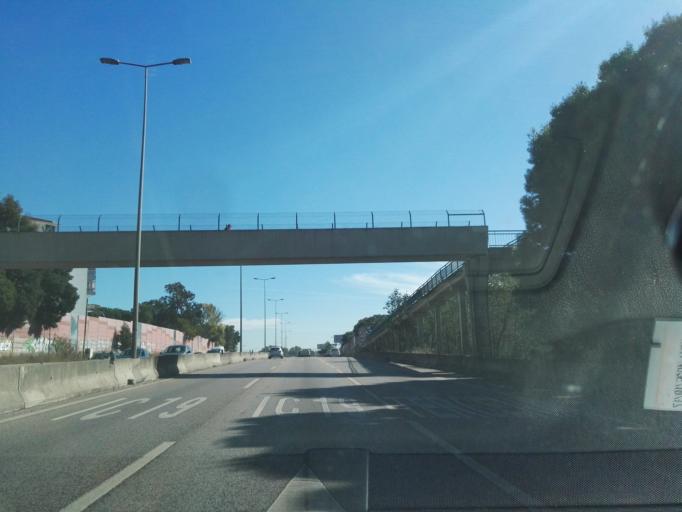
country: PT
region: Lisbon
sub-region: Sintra
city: Cacem
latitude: 38.7516
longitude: -9.2876
